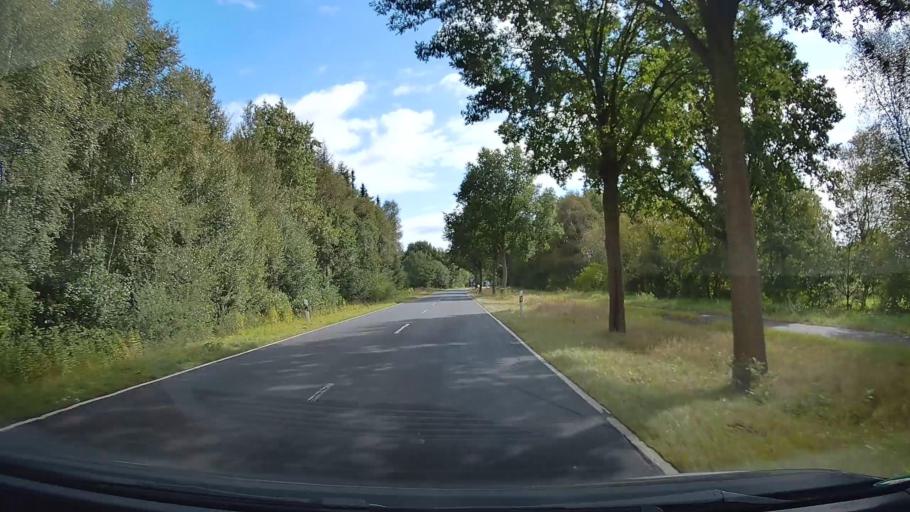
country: DE
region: Lower Saxony
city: Rhade
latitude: 53.3387
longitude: 9.1015
